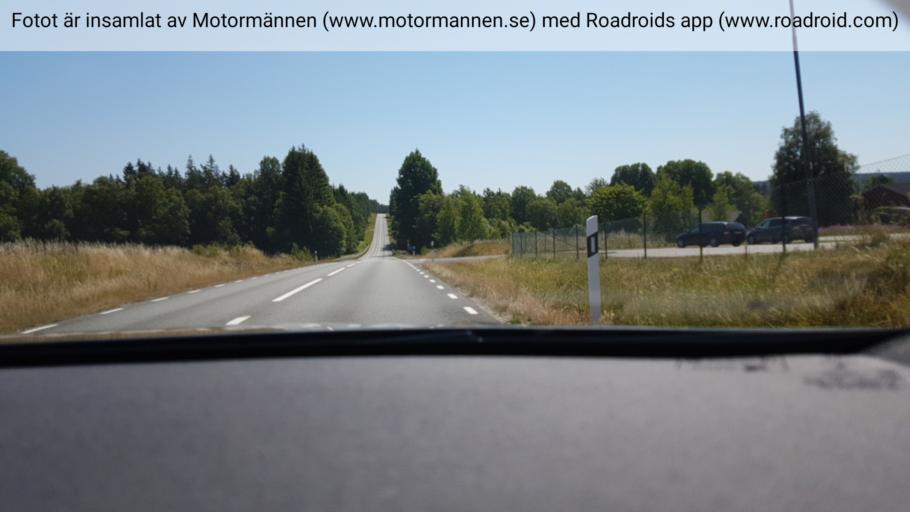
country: SE
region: Joenkoeping
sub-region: Gnosjo Kommun
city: Gnosjoe
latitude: 57.4115
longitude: 13.6435
